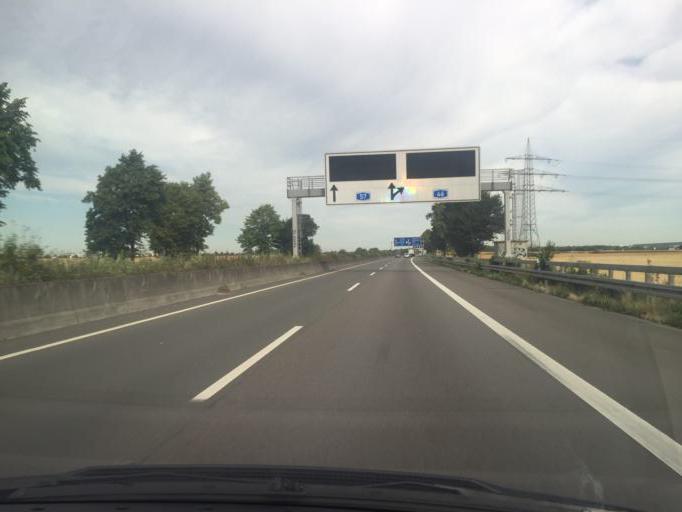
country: DE
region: North Rhine-Westphalia
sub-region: Regierungsbezirk Dusseldorf
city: Dusseldorf
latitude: 51.1435
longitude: 6.7682
